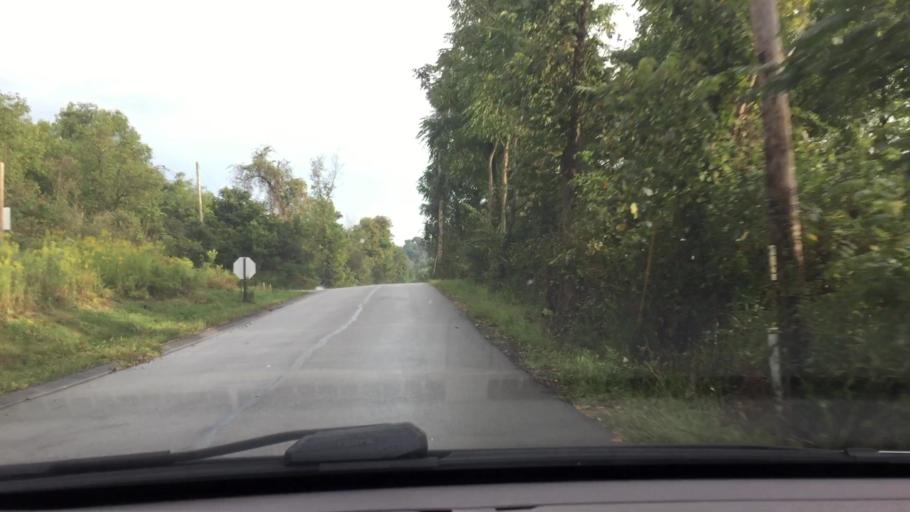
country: US
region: Pennsylvania
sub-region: Washington County
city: McGovern
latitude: 40.1895
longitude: -80.1669
